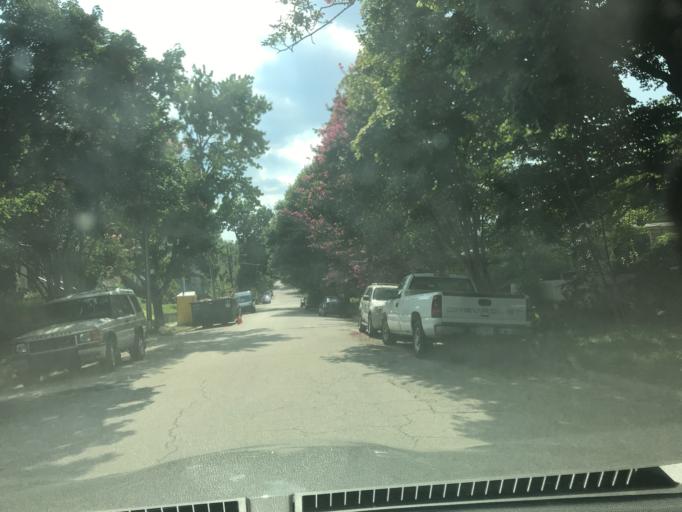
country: US
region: North Carolina
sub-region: Wake County
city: Raleigh
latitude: 35.7880
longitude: -78.6306
